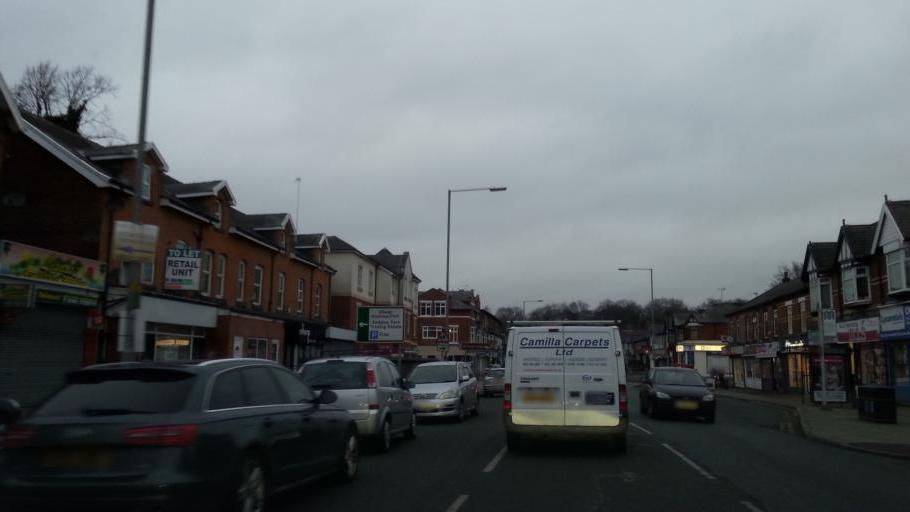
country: GB
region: England
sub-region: Borough of Bury
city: Prestwich
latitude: 53.5181
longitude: -2.2717
